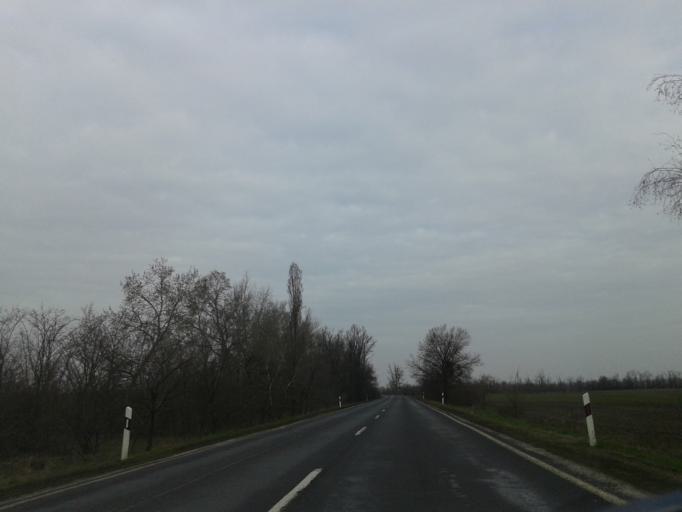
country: HU
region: Komarom-Esztergom
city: Dunaalmas
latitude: 47.7062
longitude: 18.2942
